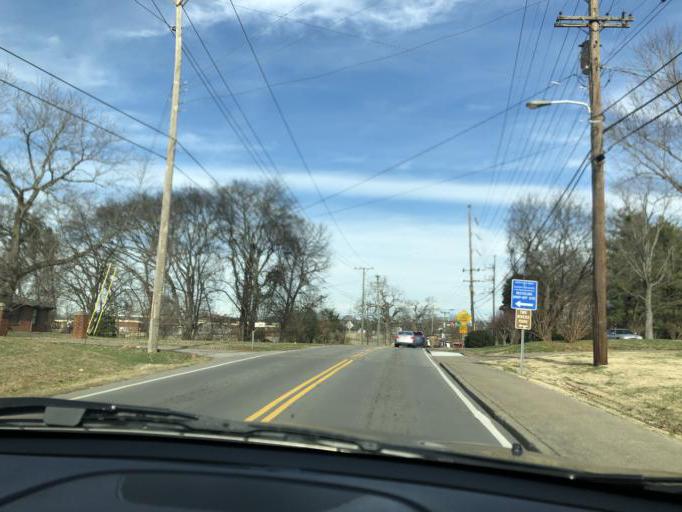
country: US
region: Tennessee
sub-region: Davidson County
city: Lakewood
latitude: 36.1821
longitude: -86.6778
